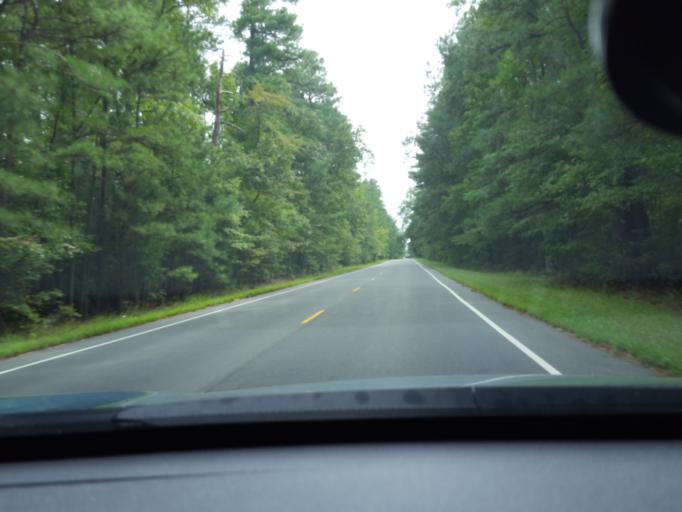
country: US
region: Virginia
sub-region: Caroline County
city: Bowling Green
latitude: 37.9777
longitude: -77.3400
